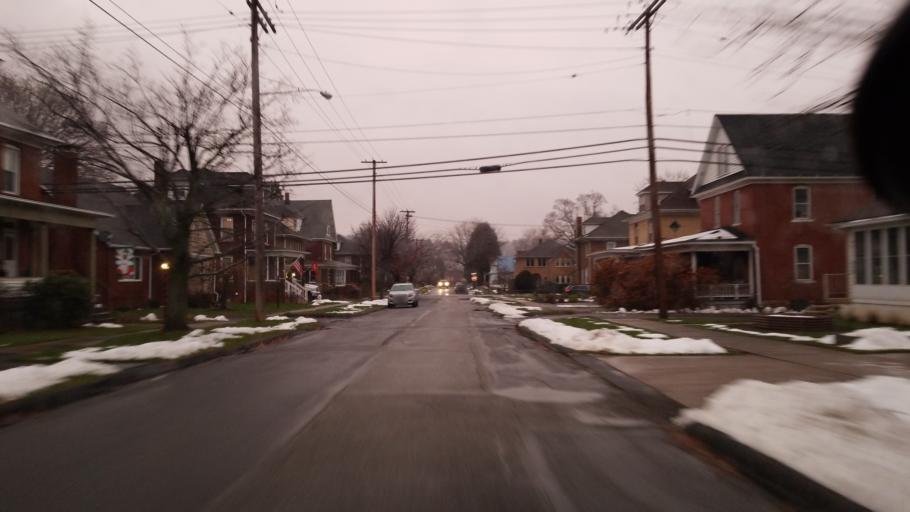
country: US
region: Pennsylvania
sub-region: Clearfield County
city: Clearfield
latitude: 41.0245
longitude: -78.4447
